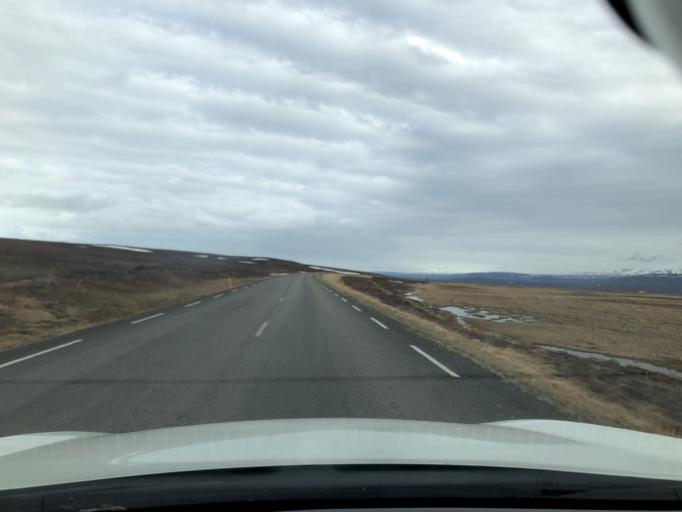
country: IS
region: Northeast
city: Laugar
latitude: 65.7162
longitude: -17.4717
